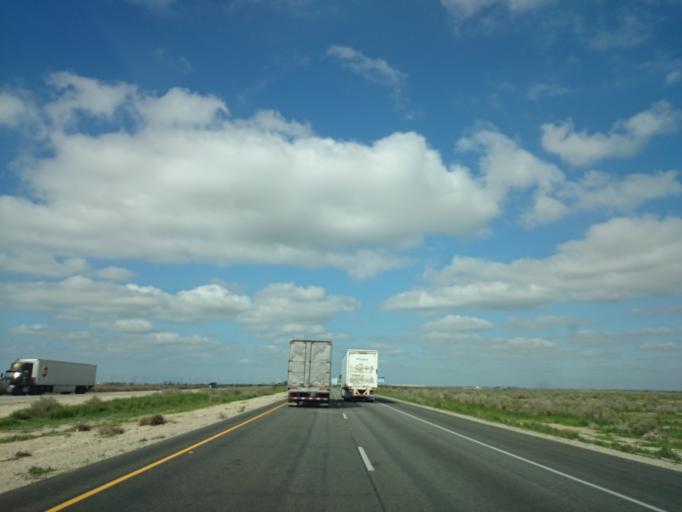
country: US
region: California
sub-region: Kern County
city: Rosedale
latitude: 35.2542
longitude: -119.2107
